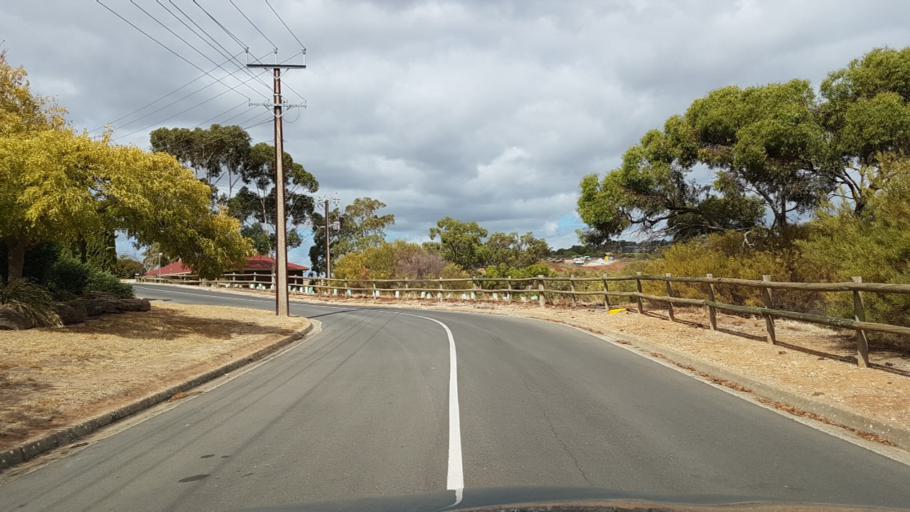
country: AU
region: South Australia
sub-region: Gawler
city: Gawler
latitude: -34.6102
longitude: 138.7539
